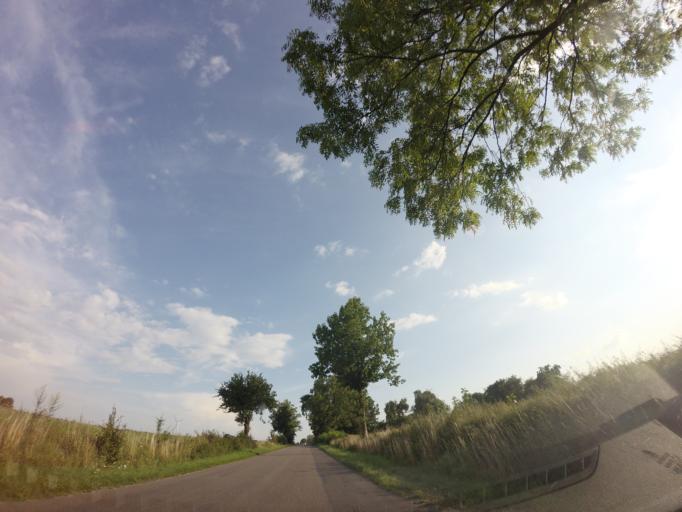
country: PL
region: Lublin Voivodeship
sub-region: Powiat lubartowski
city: Michow
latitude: 51.5155
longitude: 22.3106
